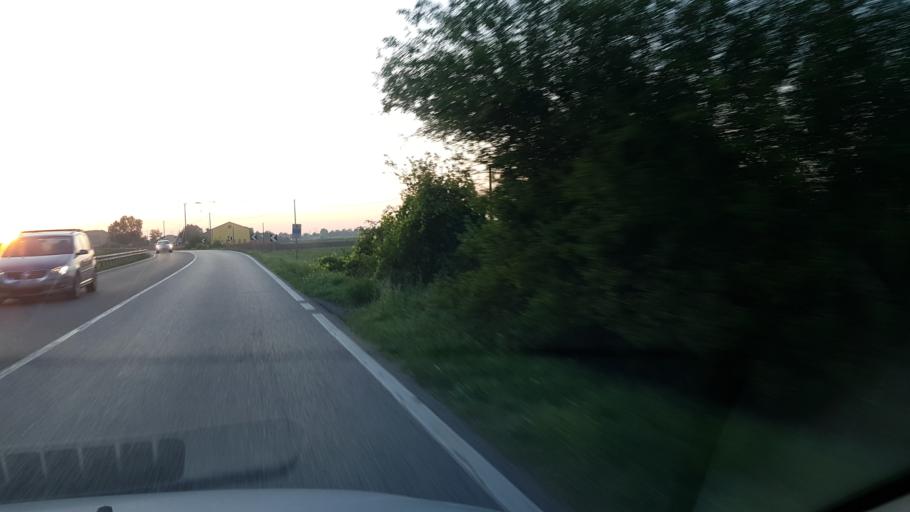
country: IT
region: Emilia-Romagna
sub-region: Provincia di Modena
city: Solara
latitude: 44.8084
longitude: 11.0799
